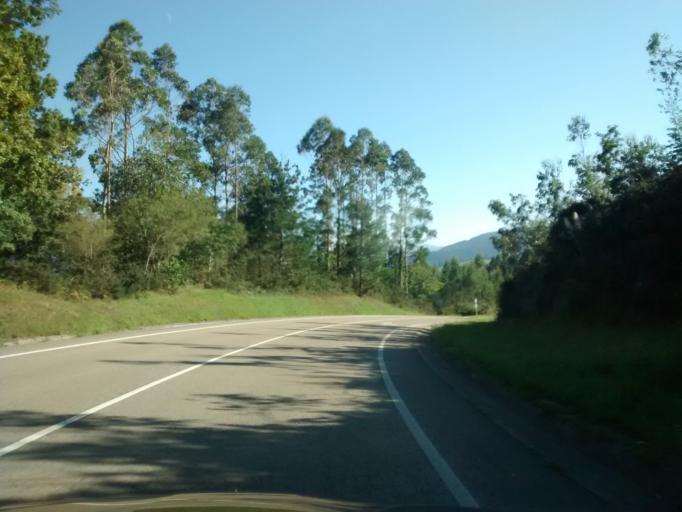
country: ES
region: Cantabria
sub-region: Provincia de Cantabria
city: Cabezon de la Sal
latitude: 43.3270
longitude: -4.2605
